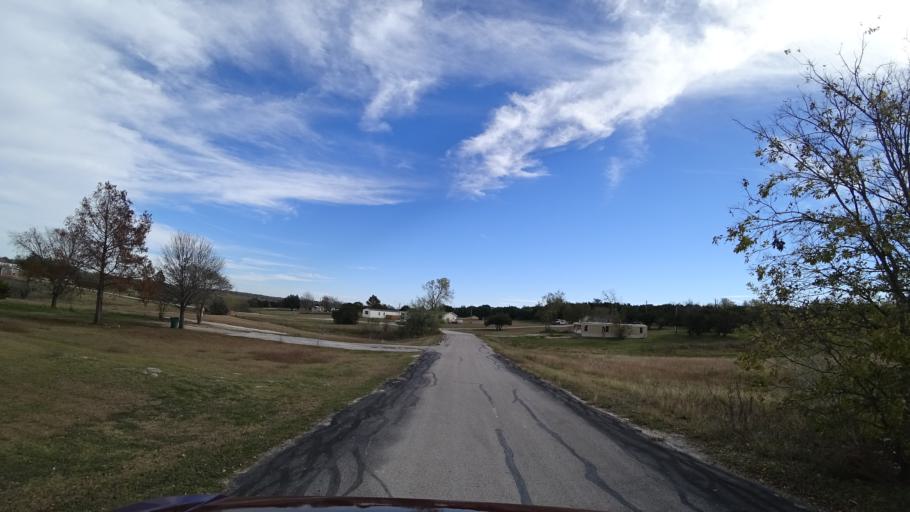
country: US
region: Texas
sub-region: Travis County
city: Onion Creek
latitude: 30.1131
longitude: -97.7321
